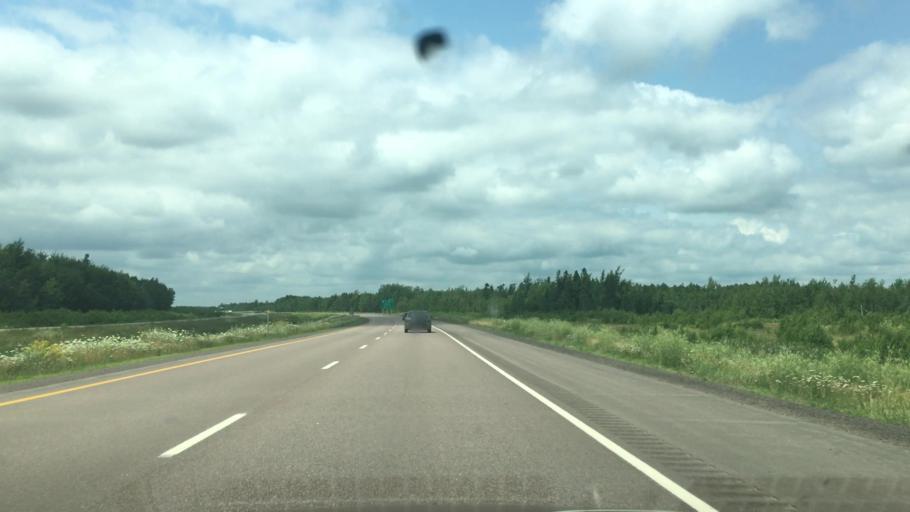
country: CA
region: New Brunswick
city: Dieppe
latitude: 46.1269
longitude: -64.6421
